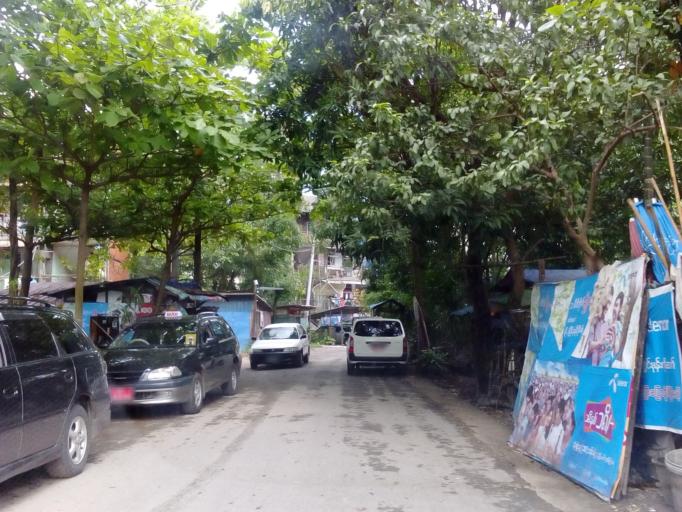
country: MM
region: Yangon
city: Yangon
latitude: 16.8262
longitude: 96.1586
